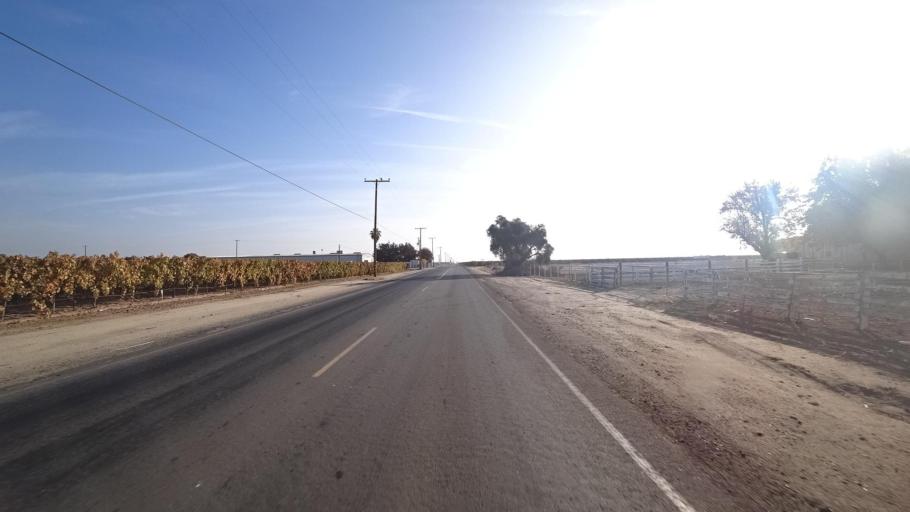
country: US
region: California
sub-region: Kern County
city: Delano
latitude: 35.7905
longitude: -119.1892
